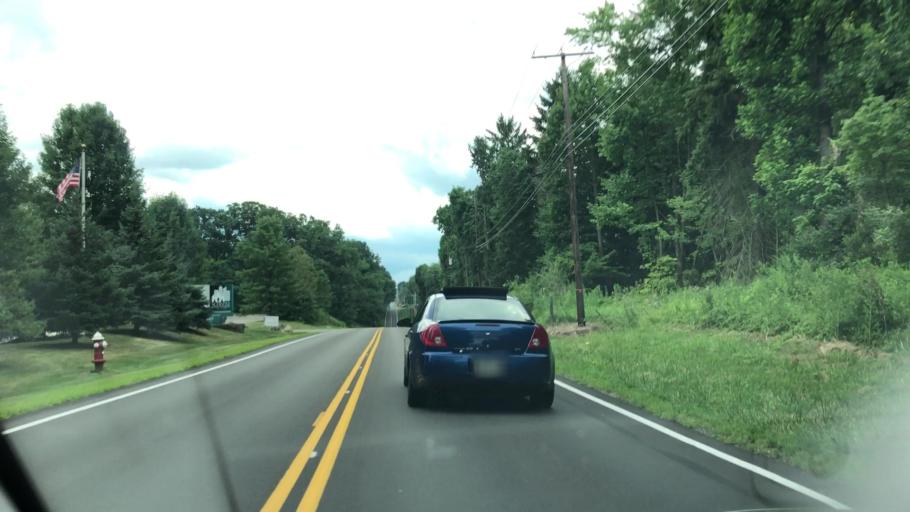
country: US
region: Ohio
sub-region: Summit County
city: Greensburg
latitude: 40.8977
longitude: -81.4404
